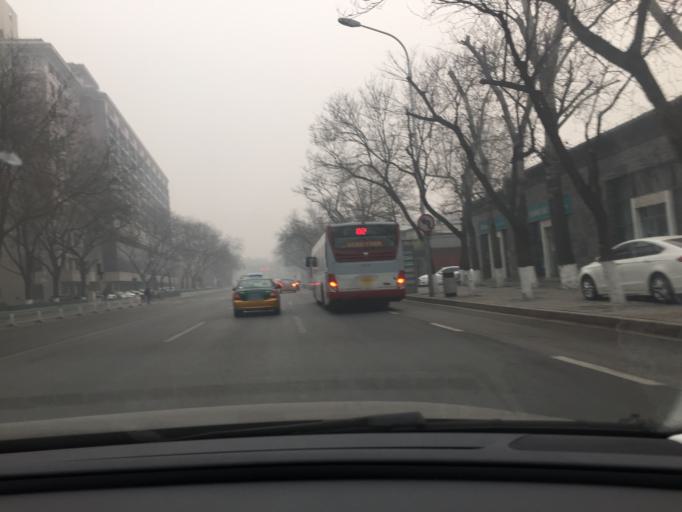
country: CN
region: Beijing
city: Beijing
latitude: 39.9088
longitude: 116.4006
